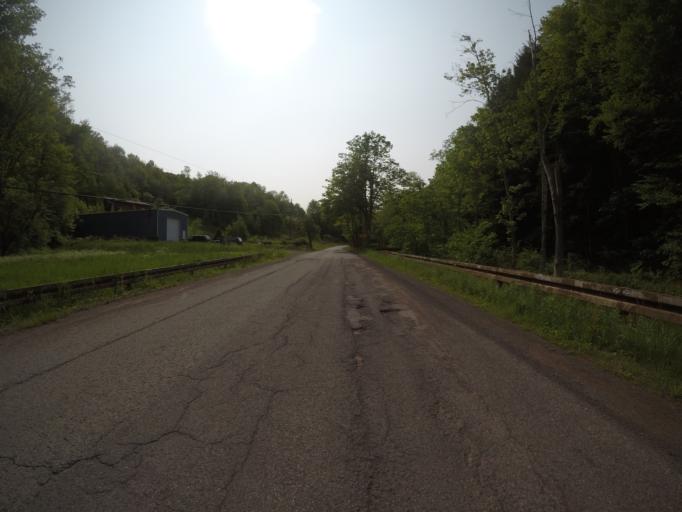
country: US
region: New York
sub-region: Sullivan County
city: Livingston Manor
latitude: 42.0825
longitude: -74.7831
